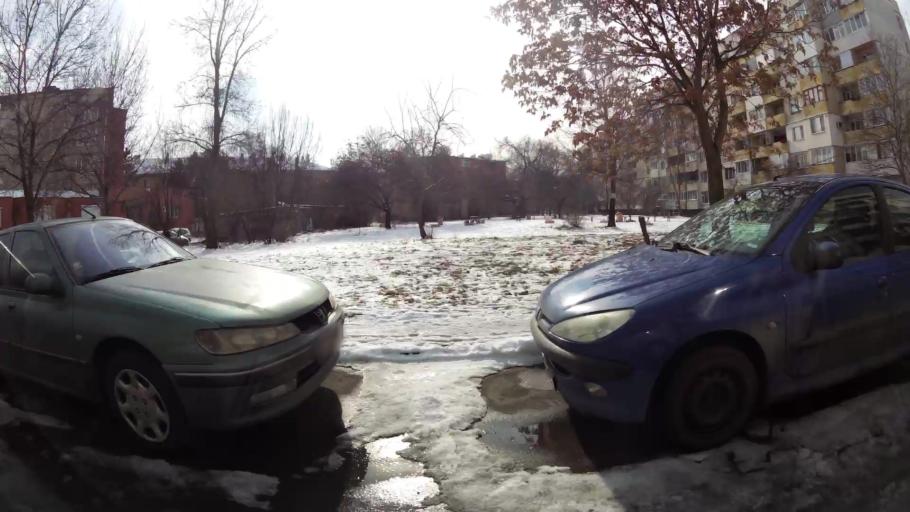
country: BG
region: Sofia-Capital
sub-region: Stolichna Obshtina
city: Sofia
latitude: 42.7053
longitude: 23.3546
